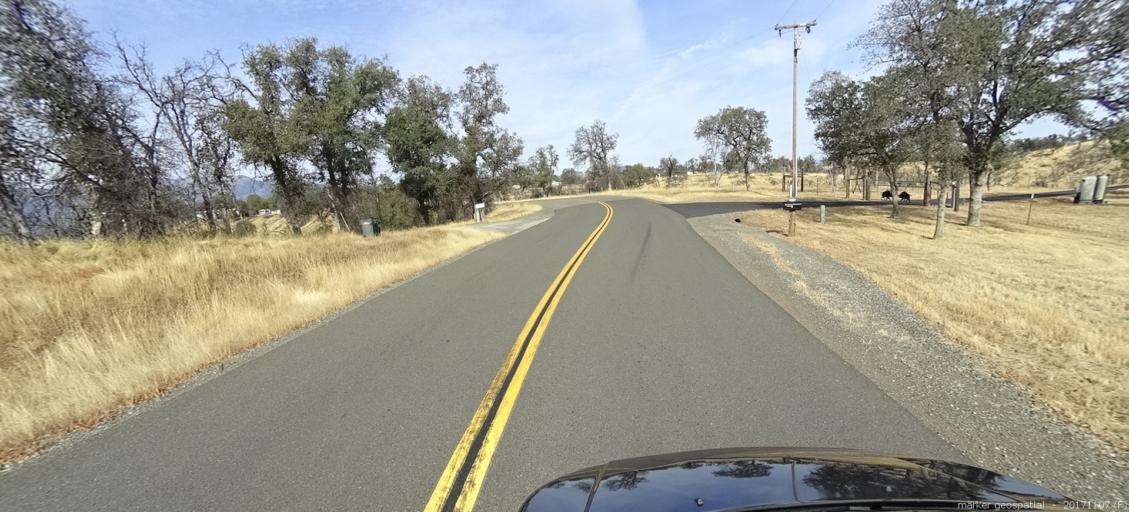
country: US
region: California
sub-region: Shasta County
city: Shasta
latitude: 40.4498
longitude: -122.5320
